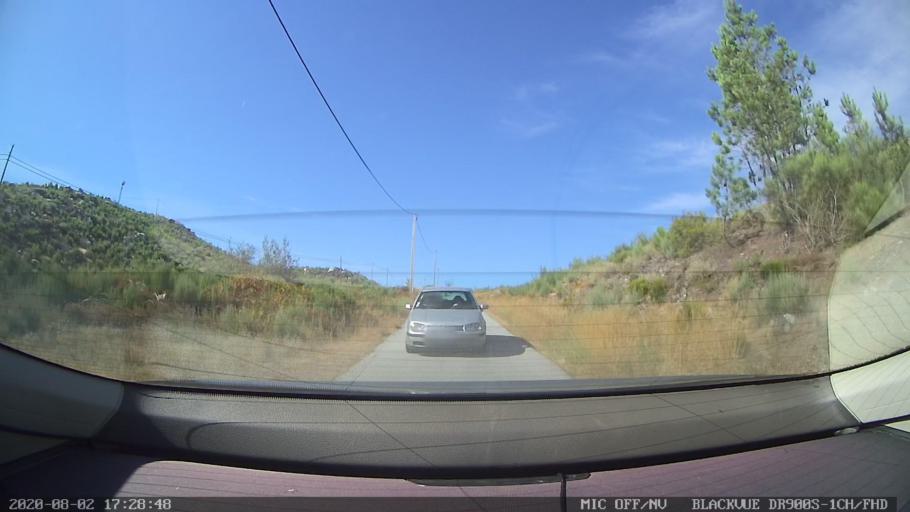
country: PT
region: Vila Real
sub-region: Sabrosa
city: Sabrosa
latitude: 41.3549
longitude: -7.5902
